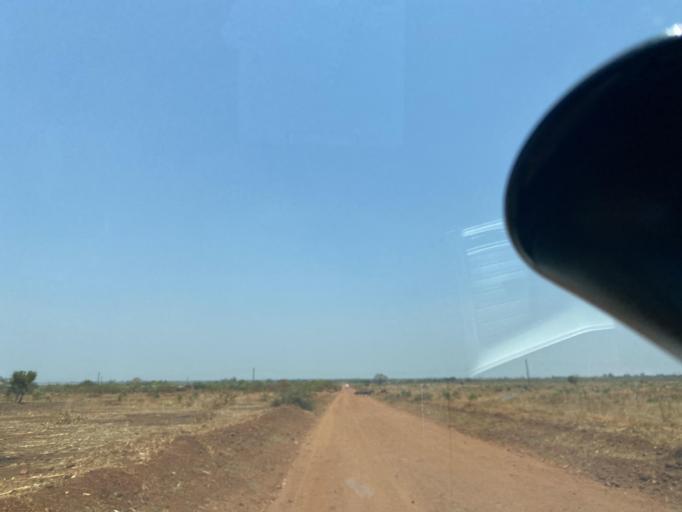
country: ZM
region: Southern
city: Nakambala
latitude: -15.5031
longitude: 27.9250
